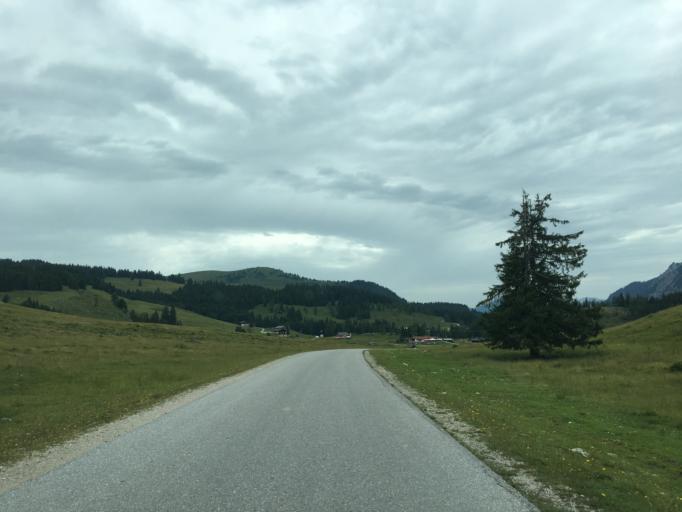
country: AT
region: Salzburg
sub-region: Politischer Bezirk Salzburg-Umgebung
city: Strobl
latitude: 47.6451
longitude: 13.4267
